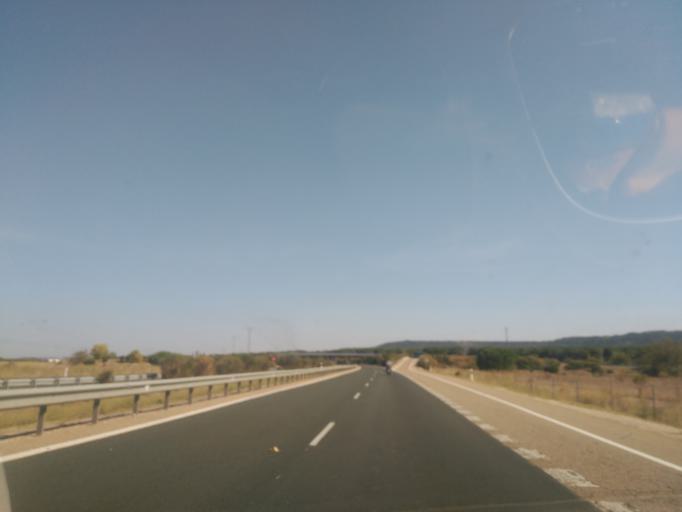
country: ES
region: Castille and Leon
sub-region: Provincia de Valladolid
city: Tudela de Duero
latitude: 41.5880
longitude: -4.5593
